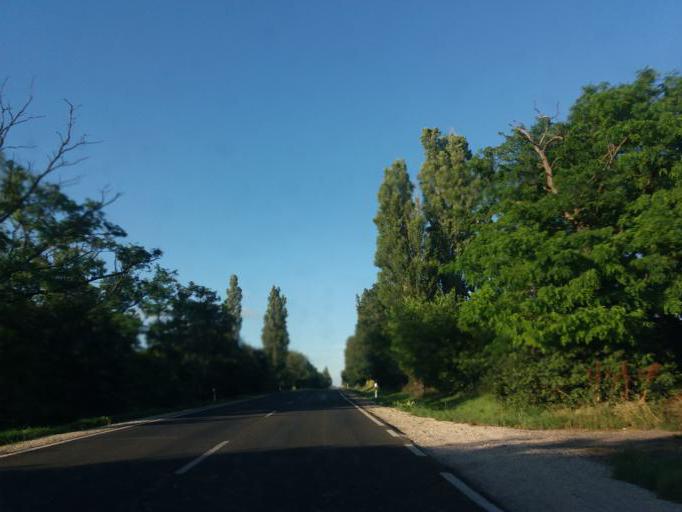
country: HU
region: Fejer
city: Baracska
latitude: 47.2687
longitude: 18.7300
